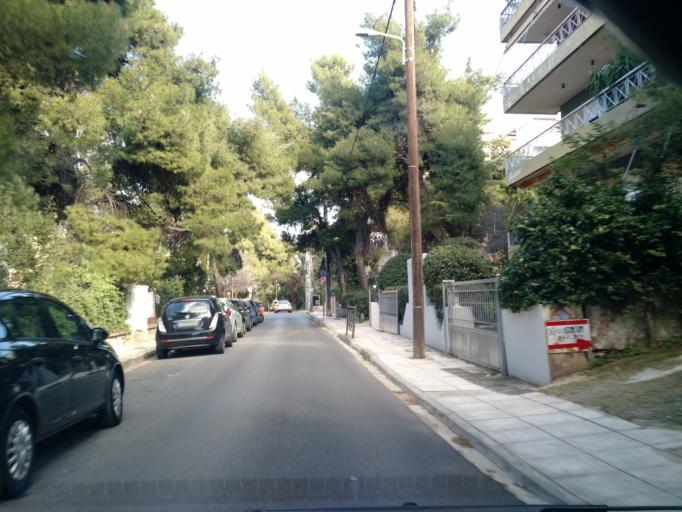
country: GR
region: Attica
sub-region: Nomarchia Athinas
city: Agia Paraskevi
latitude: 38.0089
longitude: 23.8309
